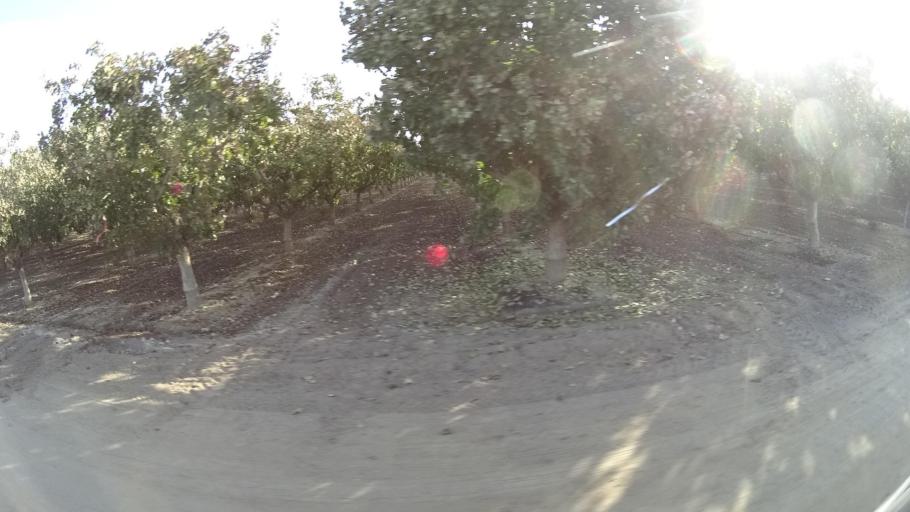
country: US
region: California
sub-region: Kern County
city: McFarland
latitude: 35.7241
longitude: -119.1872
